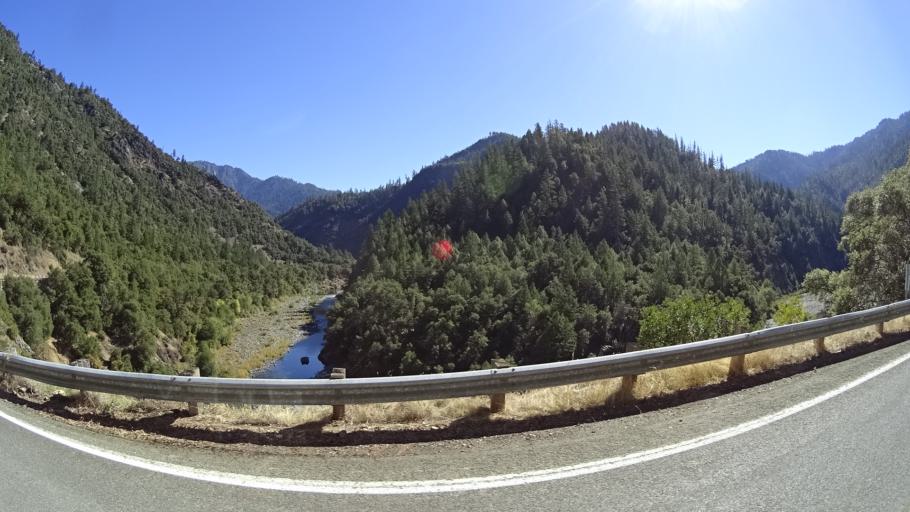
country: US
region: California
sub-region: Siskiyou County
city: Happy Camp
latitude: 41.3785
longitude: -123.4406
